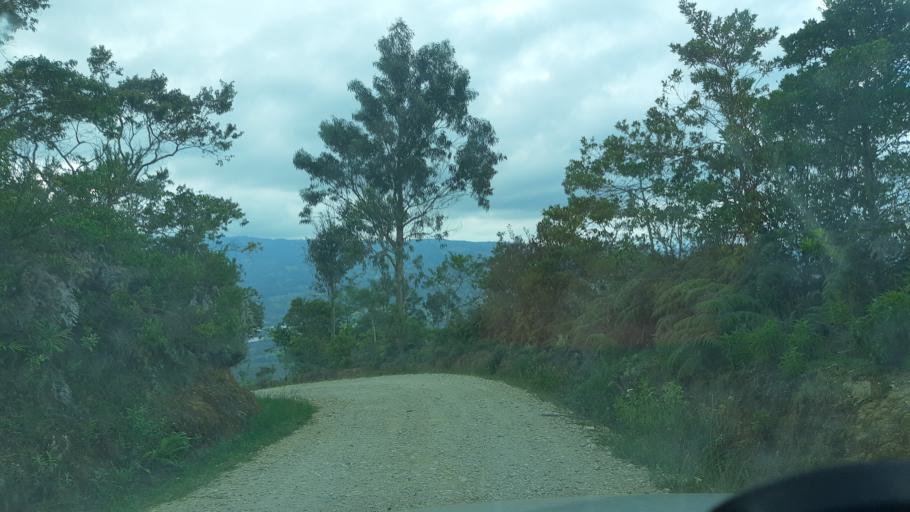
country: CO
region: Boyaca
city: Santa Sofia
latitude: 5.7445
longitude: -73.5641
